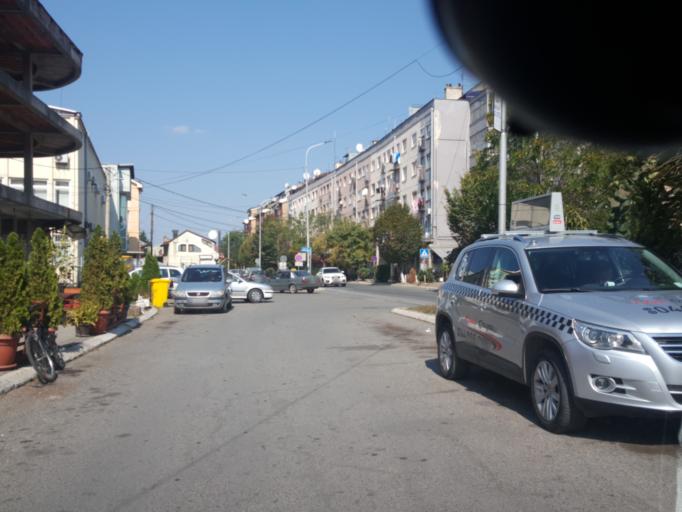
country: XK
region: Gjakova
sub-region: Komuna e Gjakoves
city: Gjakove
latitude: 42.3864
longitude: 20.4278
